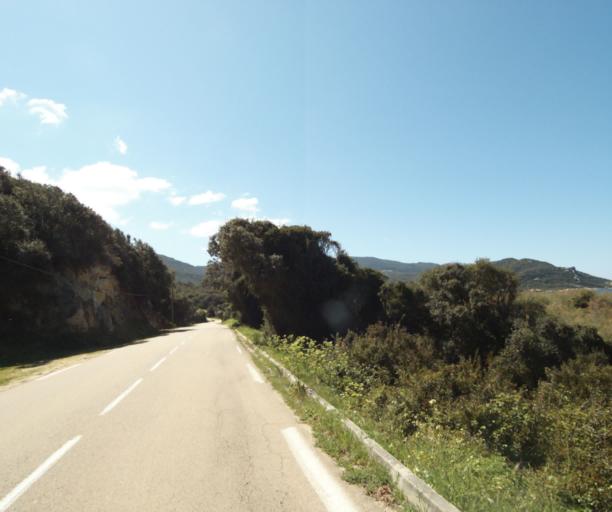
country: FR
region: Corsica
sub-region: Departement de la Corse-du-Sud
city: Propriano
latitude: 41.6510
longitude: 8.8803
